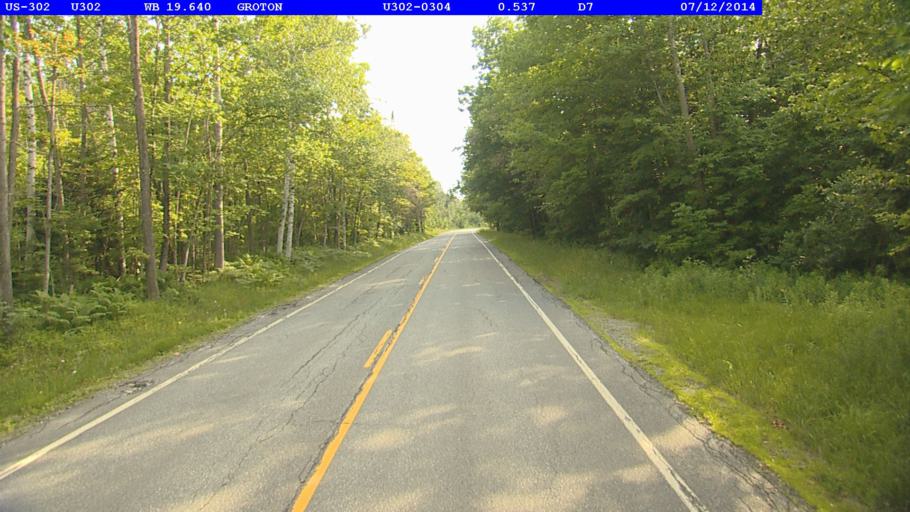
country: US
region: Vermont
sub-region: Washington County
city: Barre
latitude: 44.1889
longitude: -72.2907
